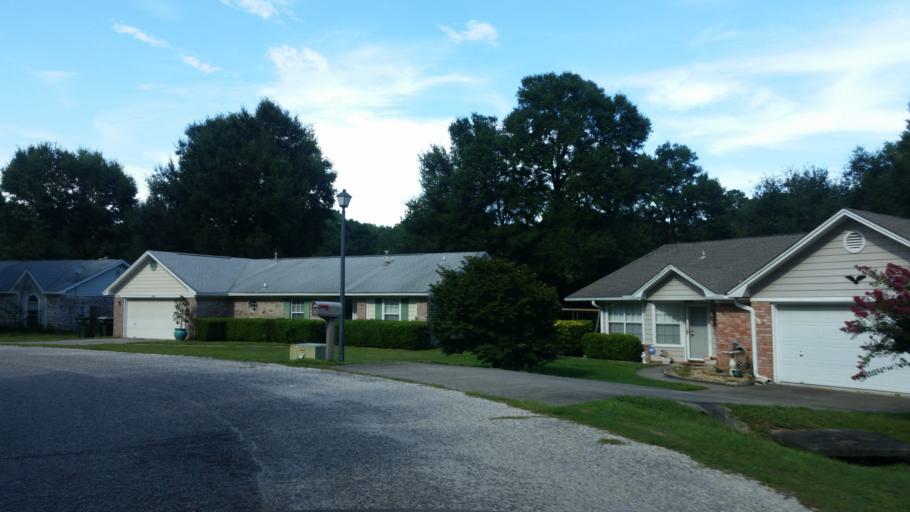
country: US
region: Florida
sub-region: Santa Rosa County
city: Pace
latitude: 30.6234
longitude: -87.1236
